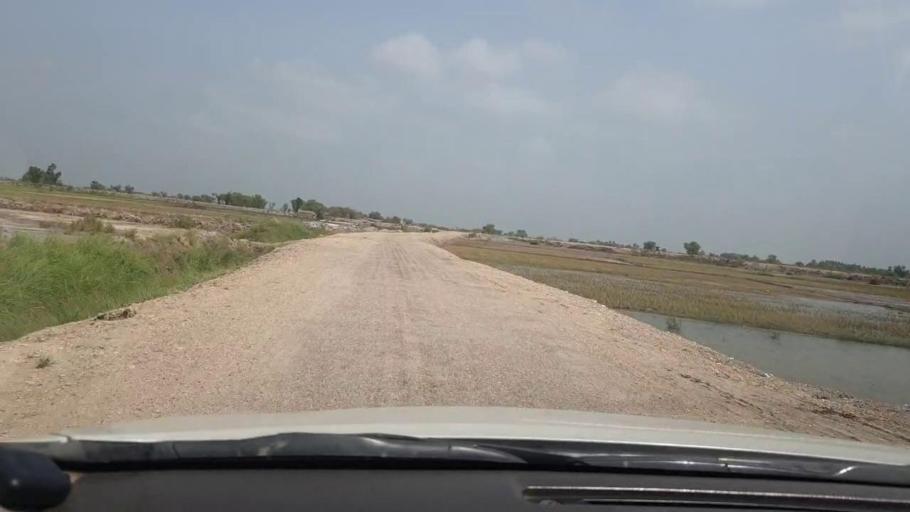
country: PK
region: Sindh
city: Shikarpur
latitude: 28.0092
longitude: 68.5569
